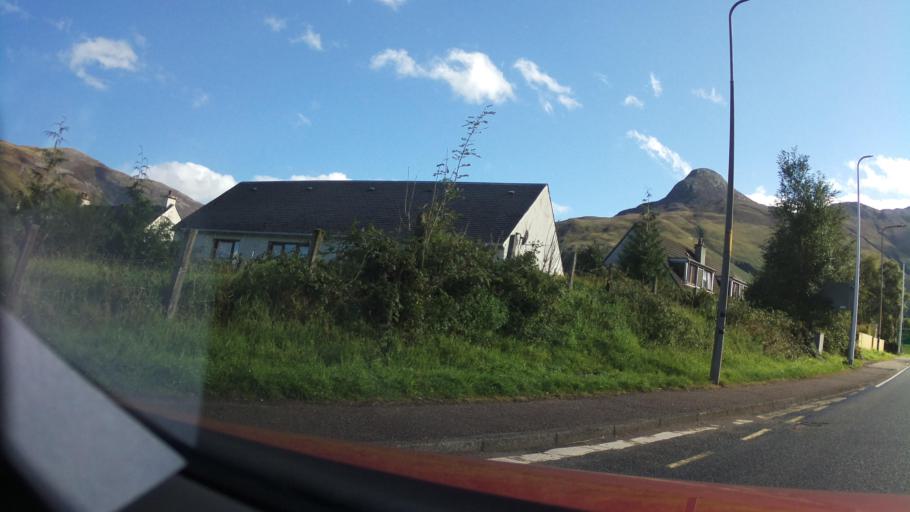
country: GB
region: Scotland
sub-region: Highland
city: Fort William
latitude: 56.6822
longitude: -5.1063
